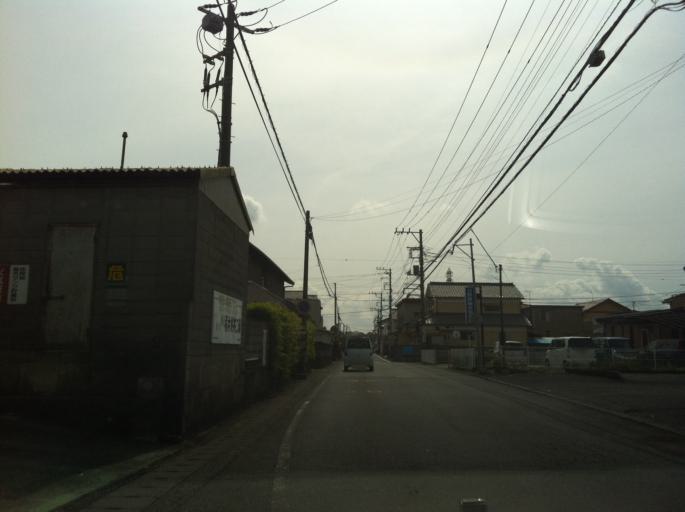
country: JP
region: Shizuoka
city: Numazu
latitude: 35.1377
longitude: 138.8116
